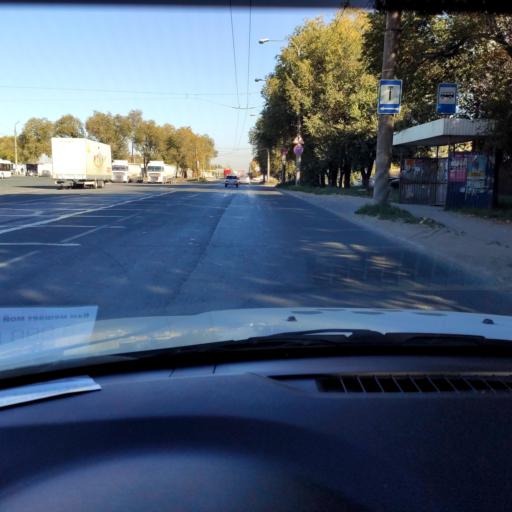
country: RU
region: Samara
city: Tol'yatti
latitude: 53.5673
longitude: 49.4577
